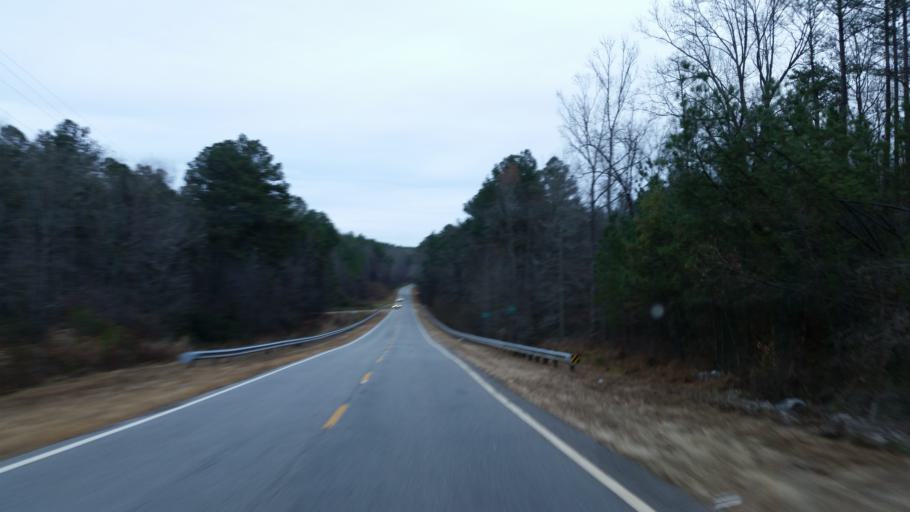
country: US
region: Georgia
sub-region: Dawson County
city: Dawsonville
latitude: 34.4519
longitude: -84.1272
